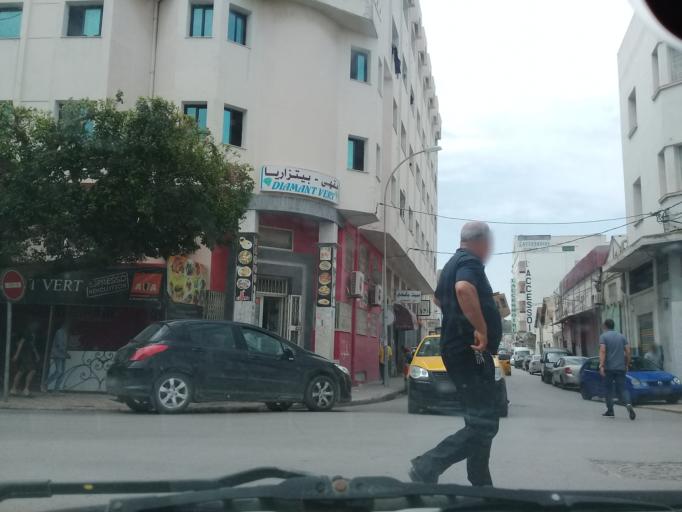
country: TN
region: Tunis
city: Tunis
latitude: 36.7922
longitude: 10.1835
